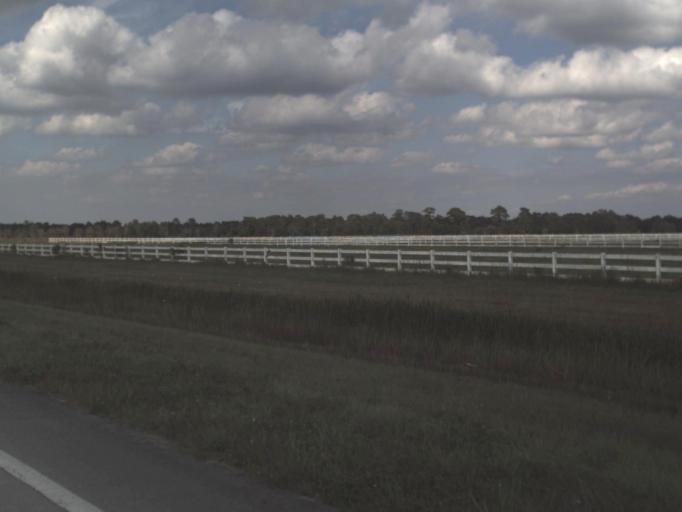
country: US
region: Florida
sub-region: Indian River County
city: Fellsmere
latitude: 27.5980
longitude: -80.8466
